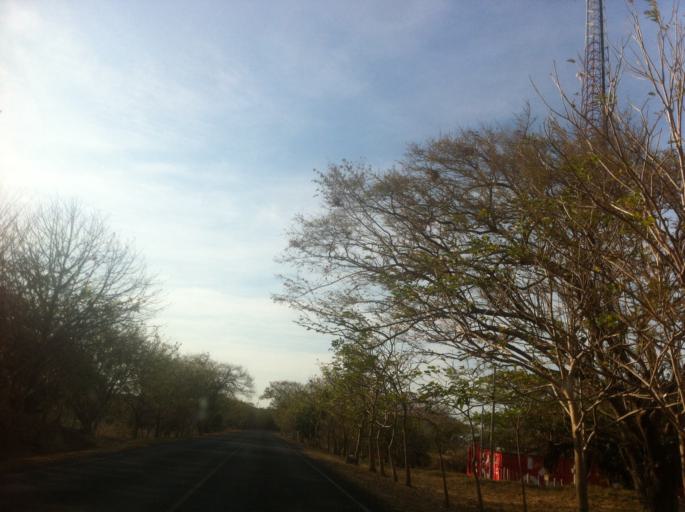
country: NI
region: Rivas
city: San Juan del Sur
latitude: 11.2928
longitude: -85.6821
